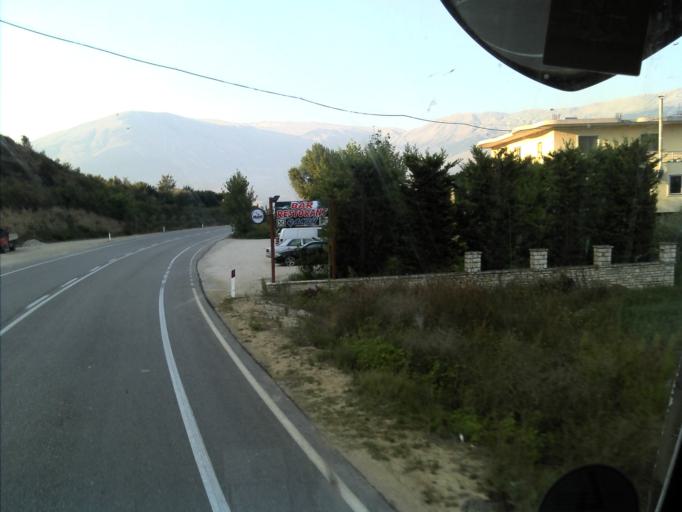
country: AL
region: Gjirokaster
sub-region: Rrethi i Tepelenes
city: Krahes
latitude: 40.4131
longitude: 19.8599
